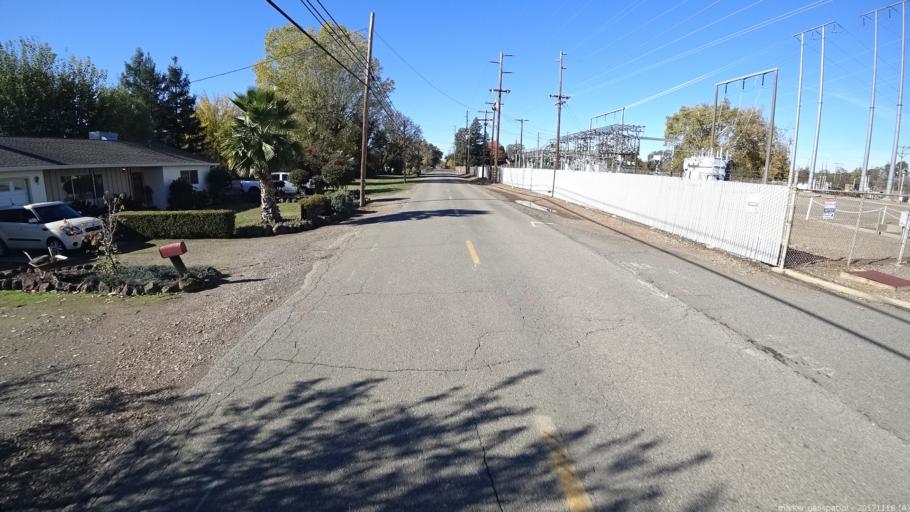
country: US
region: California
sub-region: Shasta County
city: Cottonwood
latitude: 40.3966
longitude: -122.2669
